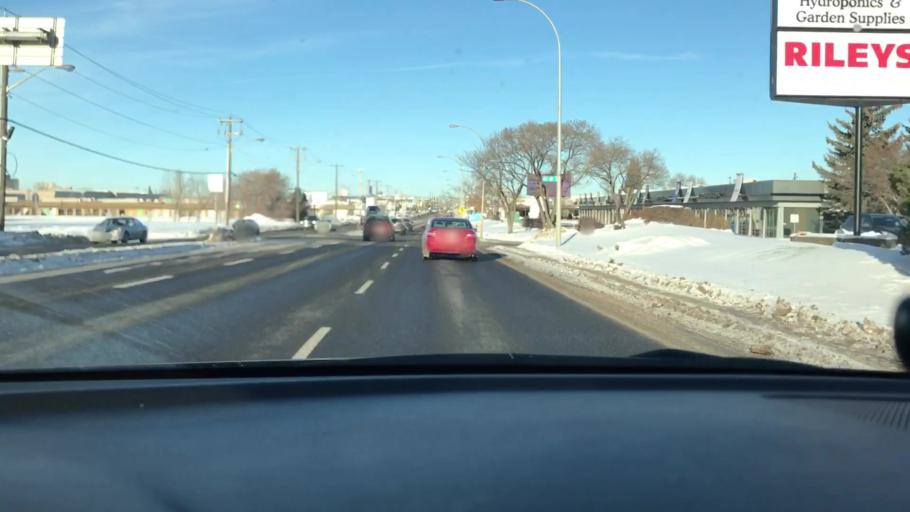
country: CA
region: Alberta
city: Edmonton
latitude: 53.4814
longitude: -113.4860
